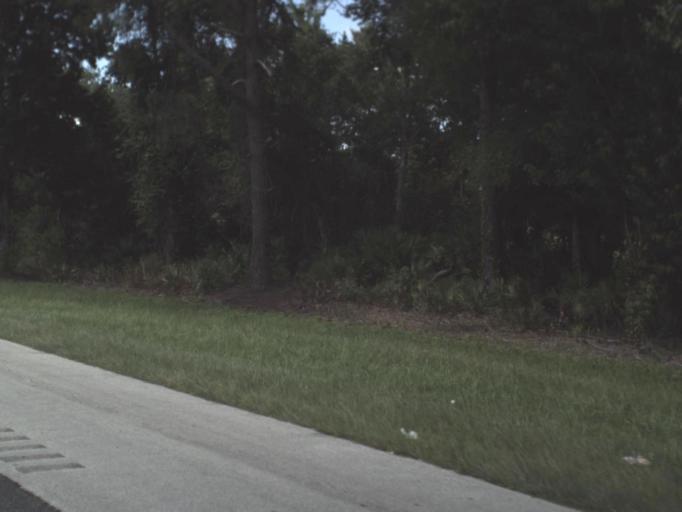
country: US
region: Florida
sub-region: Saint Johns County
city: Saint Augustine
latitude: 29.9071
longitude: -81.4090
